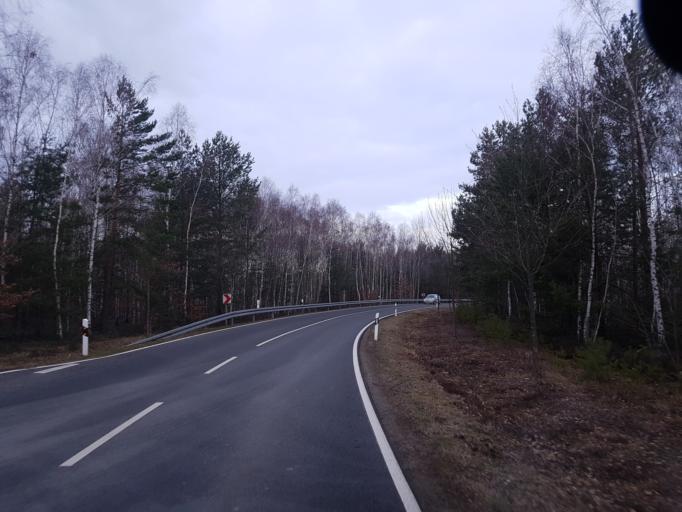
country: DE
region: Brandenburg
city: Sallgast
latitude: 51.5774
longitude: 13.8203
